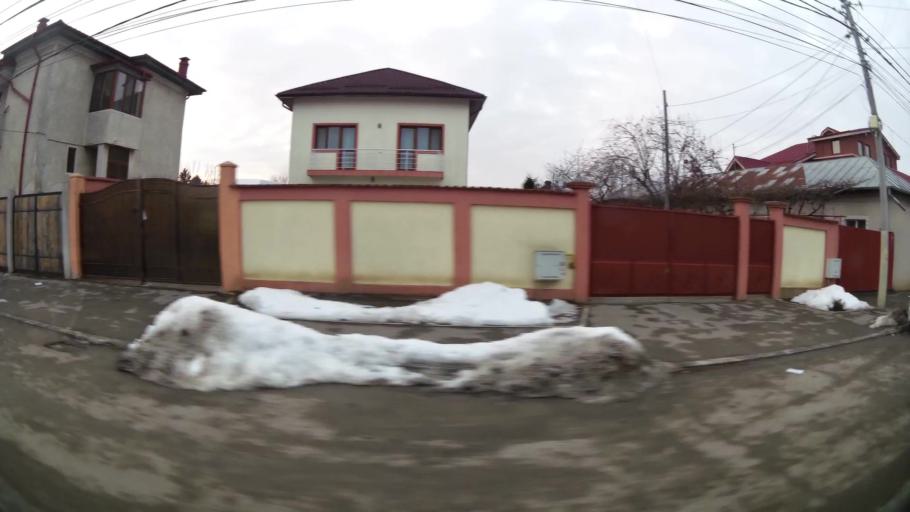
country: RO
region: Ilfov
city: Dobroesti
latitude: 44.4555
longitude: 26.1853
